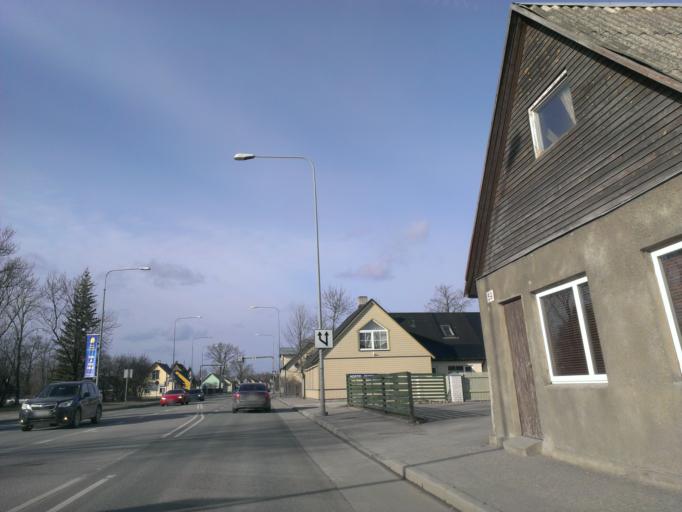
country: EE
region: Paernumaa
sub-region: Paernu linn
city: Parnu
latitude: 58.3982
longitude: 24.4936
